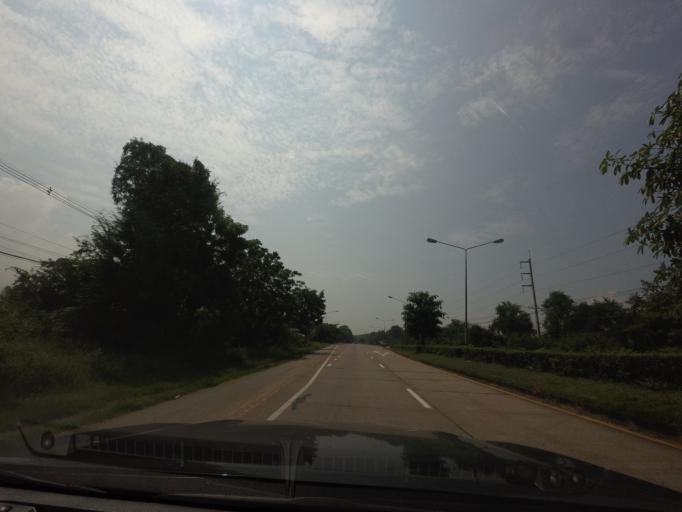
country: TH
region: Phrae
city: Sung Men
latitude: 18.0057
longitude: 100.1046
